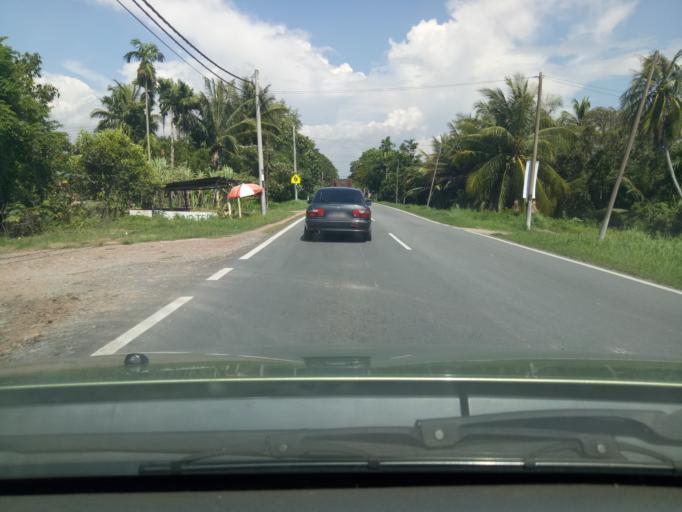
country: MY
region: Kedah
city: Alor Setar
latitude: 5.9710
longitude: 100.4180
